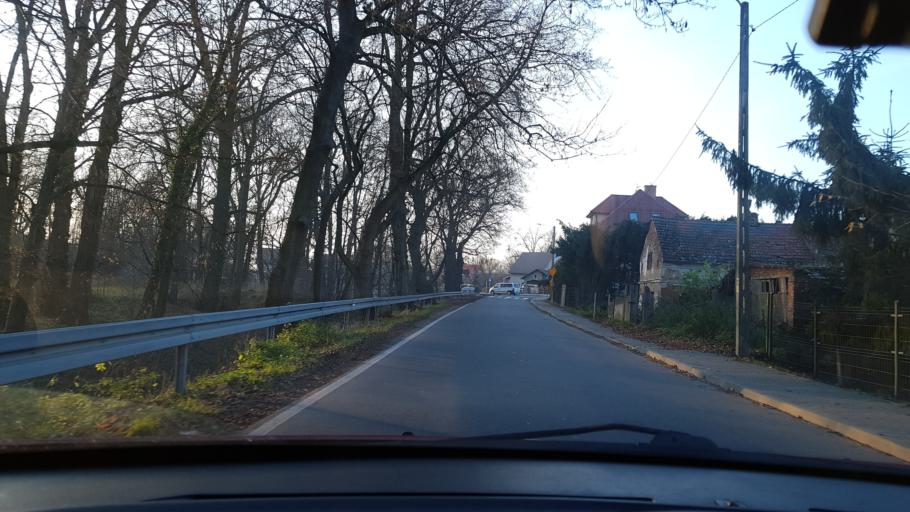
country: PL
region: Lower Silesian Voivodeship
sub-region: Powiat zabkowicki
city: Henrykow
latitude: 50.6568
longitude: 17.0141
